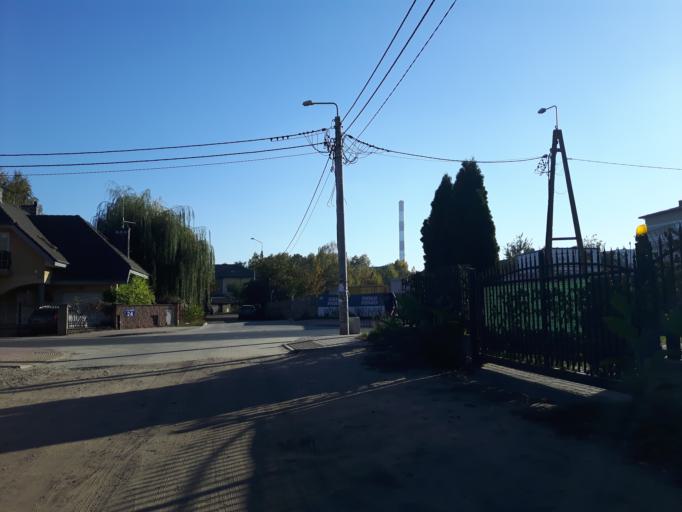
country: PL
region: Masovian Voivodeship
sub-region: Powiat wolominski
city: Zabki
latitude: 52.2827
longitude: 21.1323
